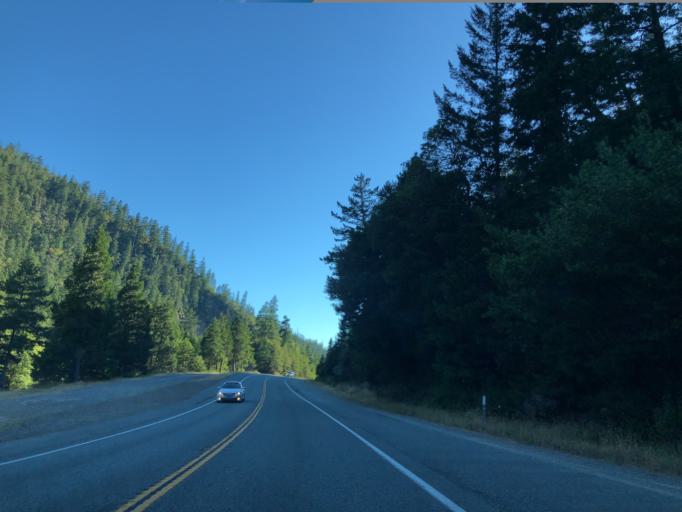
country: US
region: California
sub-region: Del Norte County
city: Bertsch-Oceanview
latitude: 41.8629
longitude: -123.8669
